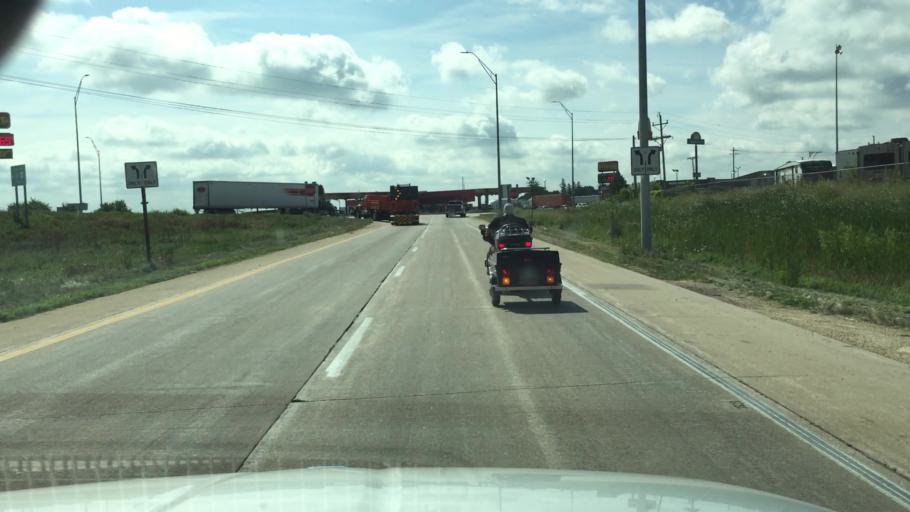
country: US
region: Iowa
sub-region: Scott County
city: Walcott
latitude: 41.6157
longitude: -90.7842
